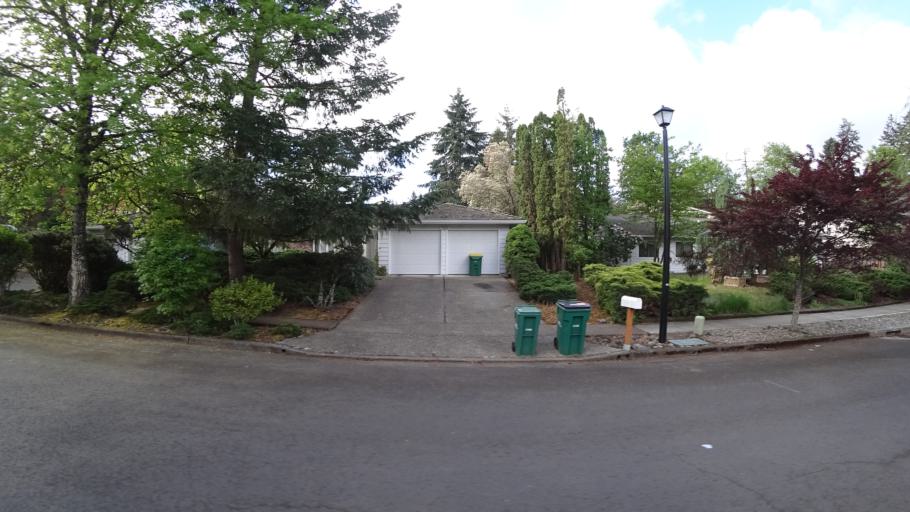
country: US
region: Oregon
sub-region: Washington County
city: Beaverton
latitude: 45.4692
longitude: -122.8202
